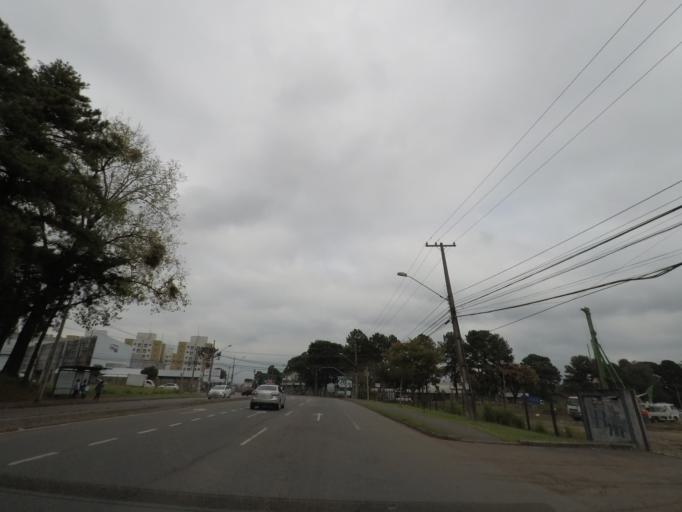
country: BR
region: Parana
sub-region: Curitiba
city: Curitiba
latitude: -25.4945
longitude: -49.3248
